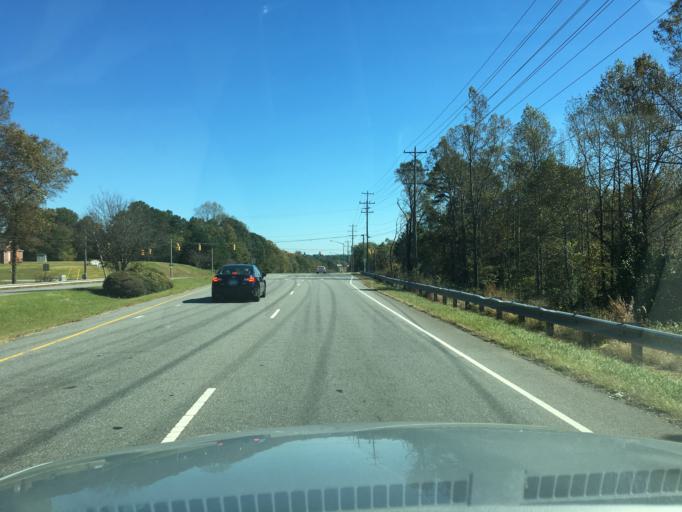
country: US
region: North Carolina
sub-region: Catawba County
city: Hickory
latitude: 35.7278
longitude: -81.3001
